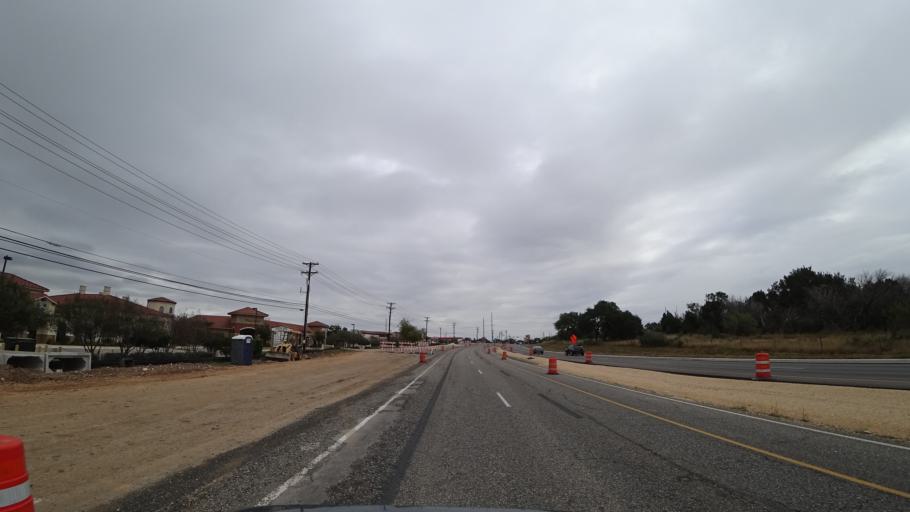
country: US
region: Texas
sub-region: Williamson County
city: Round Rock
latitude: 30.5120
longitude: -97.7048
